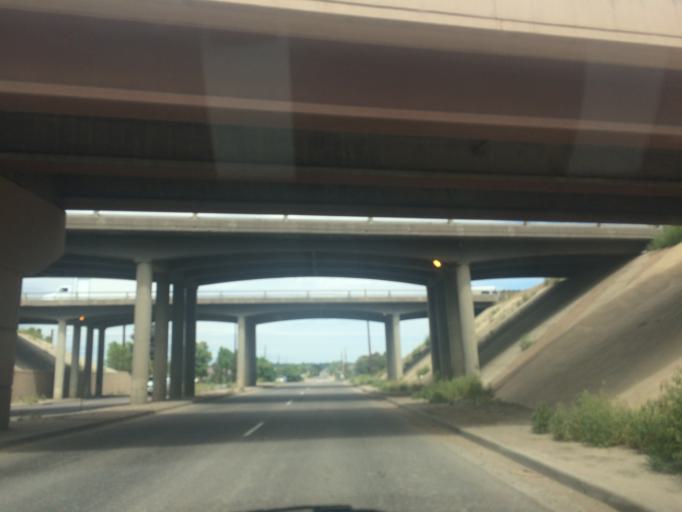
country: US
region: Colorado
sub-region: Adams County
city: Welby
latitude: 39.8239
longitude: -104.9592
